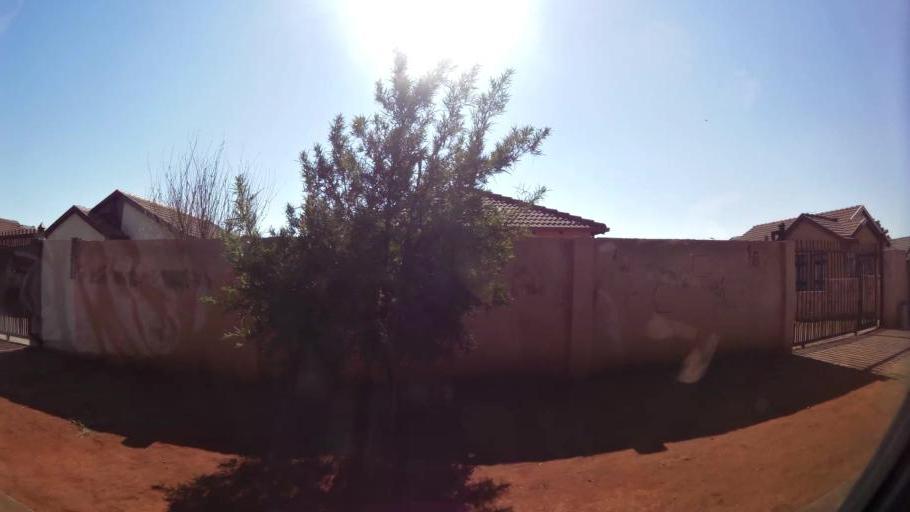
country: ZA
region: North-West
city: Ga-Rankuwa
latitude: -25.6386
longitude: 28.0811
